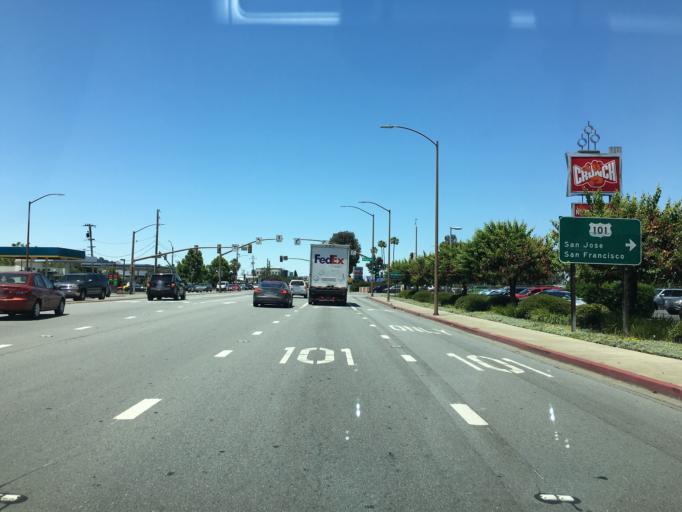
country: US
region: California
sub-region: San Mateo County
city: Redwood City
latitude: 37.4940
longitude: -122.2335
